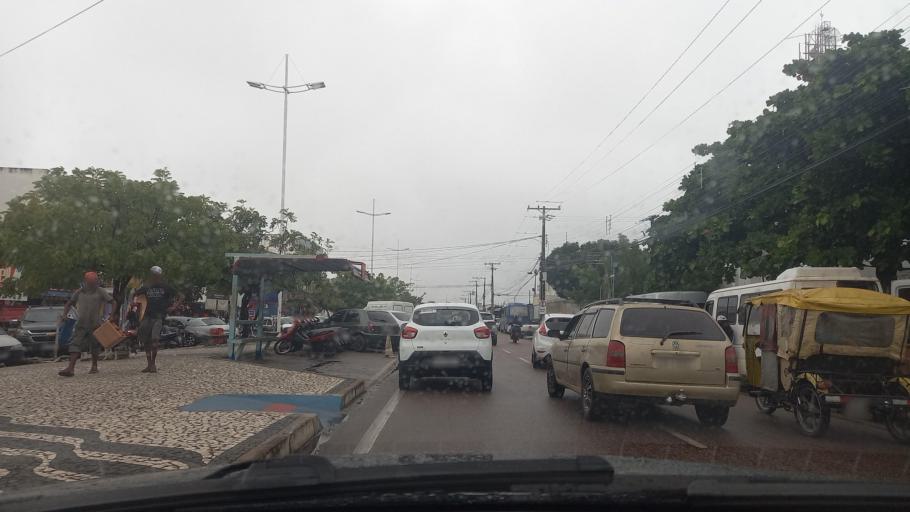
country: BR
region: Bahia
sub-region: Paulo Afonso
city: Paulo Afonso
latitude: -9.4022
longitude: -38.2293
